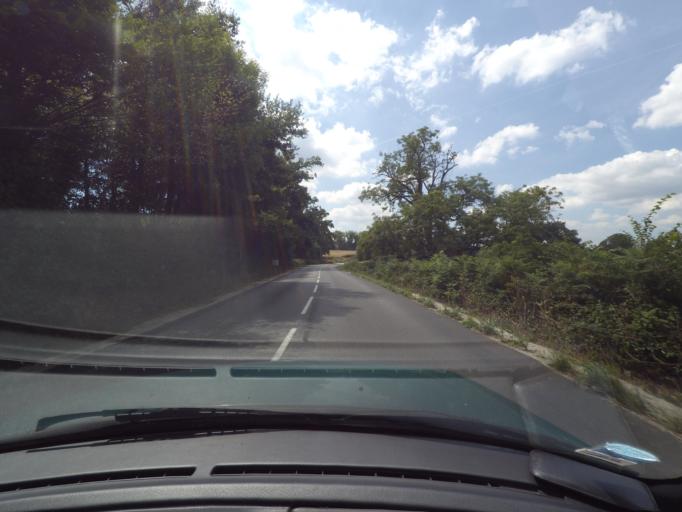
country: FR
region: Limousin
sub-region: Departement de la Haute-Vienne
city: Isle
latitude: 45.7827
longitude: 1.2257
